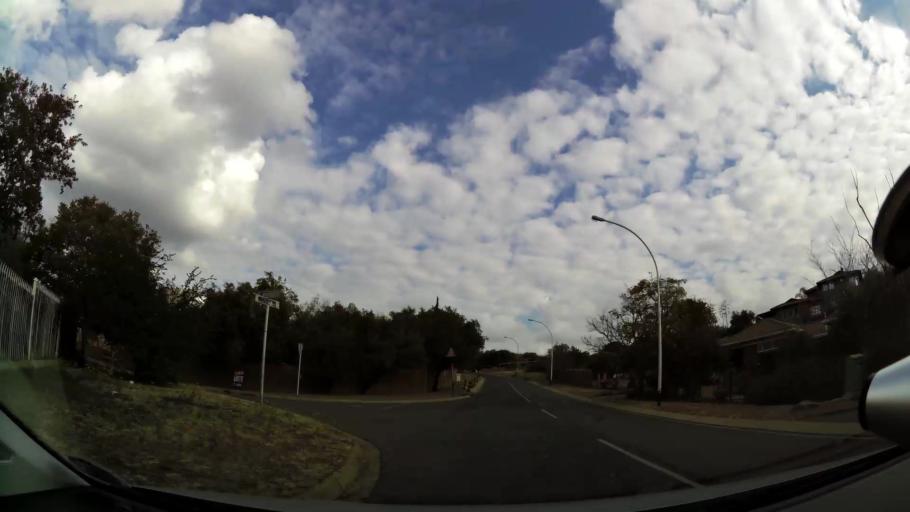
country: ZA
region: Orange Free State
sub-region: Mangaung Metropolitan Municipality
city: Bloemfontein
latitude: -29.0733
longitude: 26.2085
